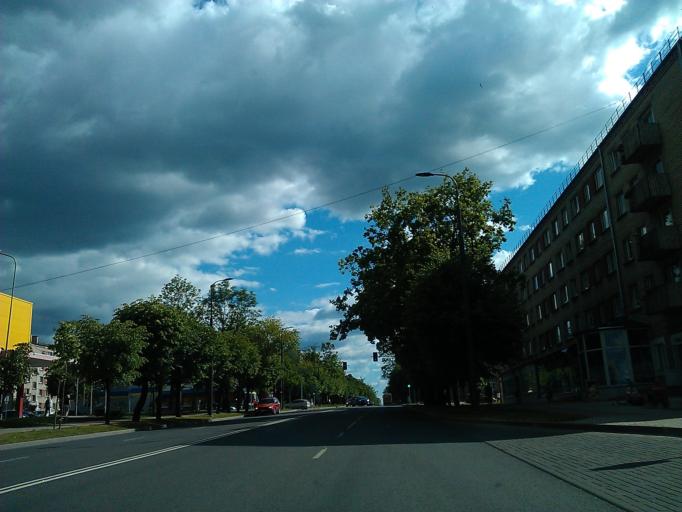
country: LV
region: Rezekne
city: Rezekne
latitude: 56.5152
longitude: 27.3360
